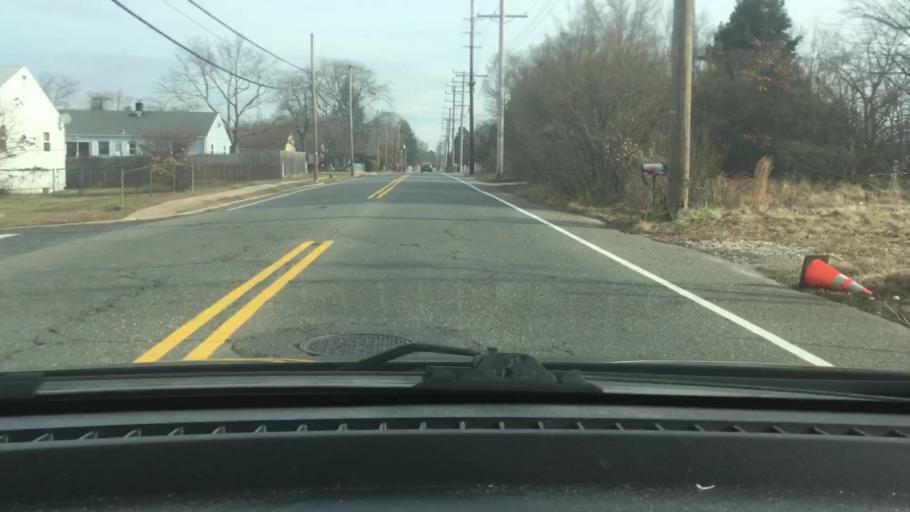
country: US
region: New Jersey
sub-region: Monmouth County
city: Shark River Hills
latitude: 40.2180
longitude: -74.0676
